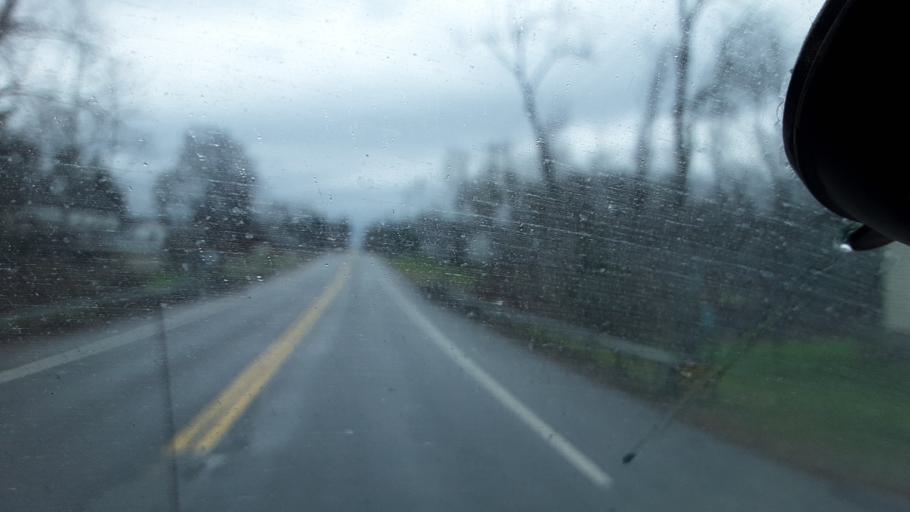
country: US
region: New York
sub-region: Erie County
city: Holland
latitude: 42.6598
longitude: -78.5545
